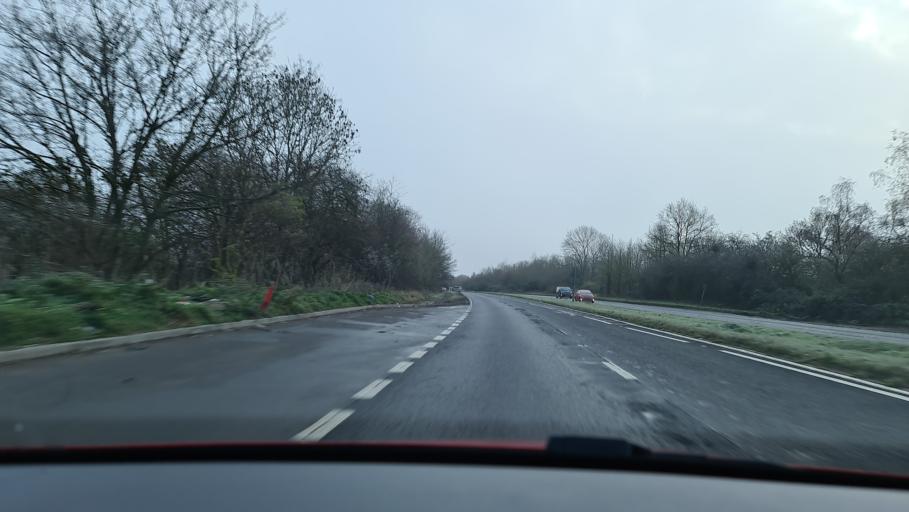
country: GB
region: England
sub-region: Buckinghamshire
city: Seer Green
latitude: 51.5995
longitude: -0.6195
